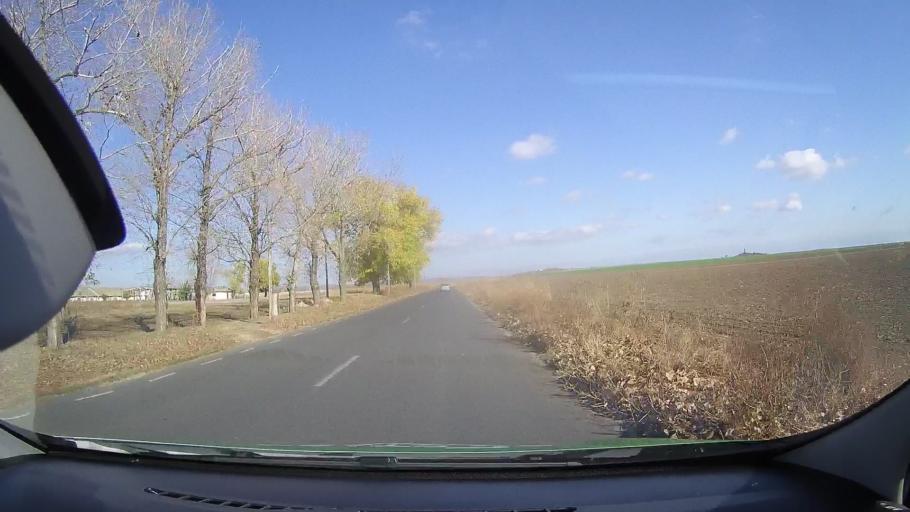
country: RO
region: Tulcea
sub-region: Comuna Baia
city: Baia
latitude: 44.7352
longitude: 28.6868
